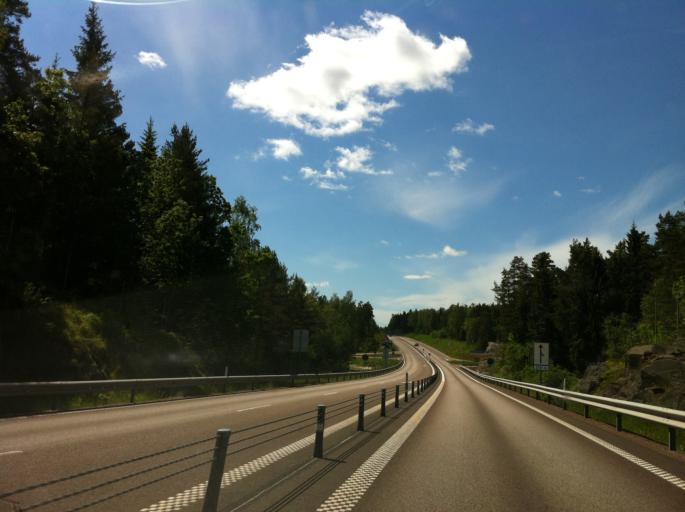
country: SE
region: Vaestra Goetaland
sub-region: Melleruds Kommun
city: Mellerud
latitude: 58.7760
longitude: 12.4997
